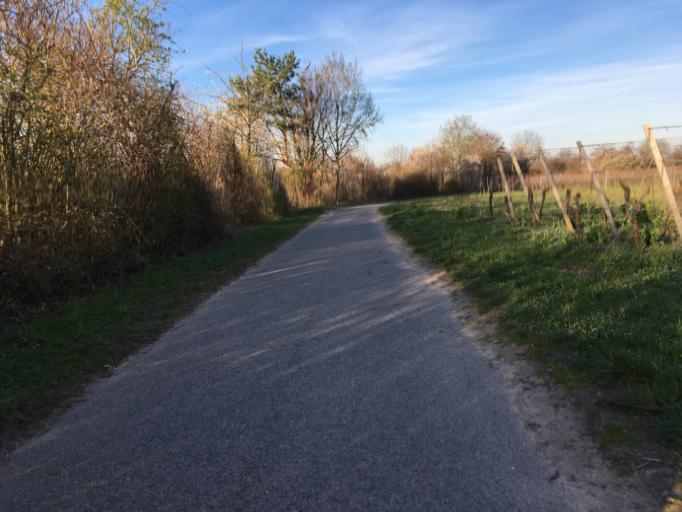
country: DE
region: Rheinland-Pfalz
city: Deidesheim
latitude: 49.3803
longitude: 8.1620
